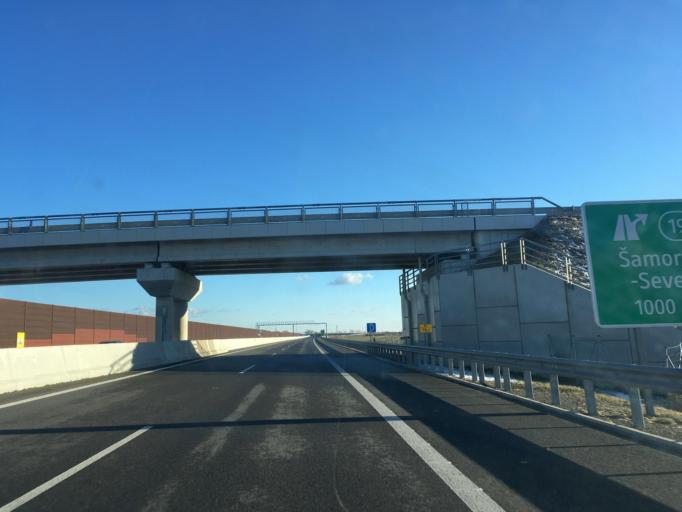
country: SK
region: Trnavsky
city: Samorin
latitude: 48.0503
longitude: 17.3246
